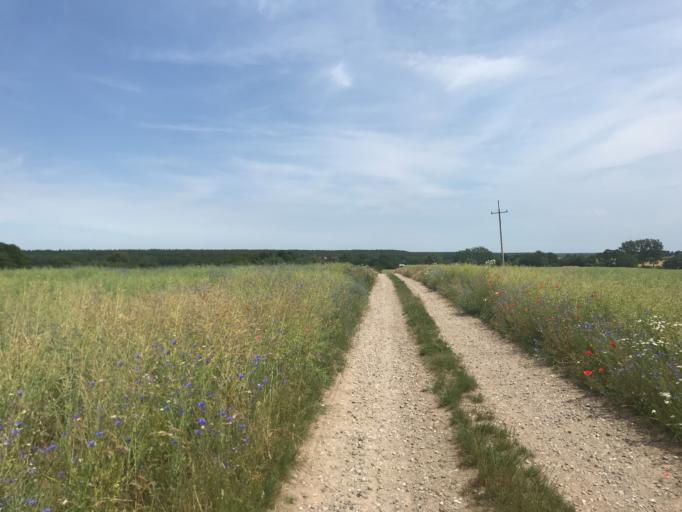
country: PL
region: West Pomeranian Voivodeship
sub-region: Powiat mysliborski
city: Boleszkowice
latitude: 52.6823
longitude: 14.6332
